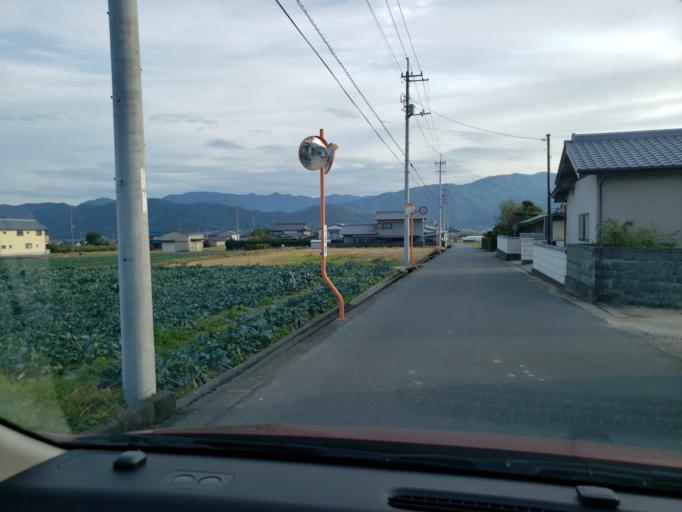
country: JP
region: Tokushima
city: Wakimachi
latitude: 34.0857
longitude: 134.2268
